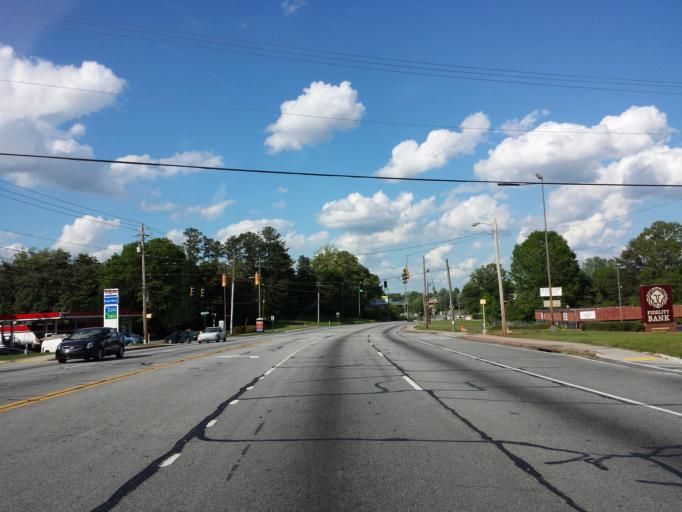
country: US
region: Georgia
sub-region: Cobb County
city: Fair Oaks
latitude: 33.9326
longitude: -84.5486
